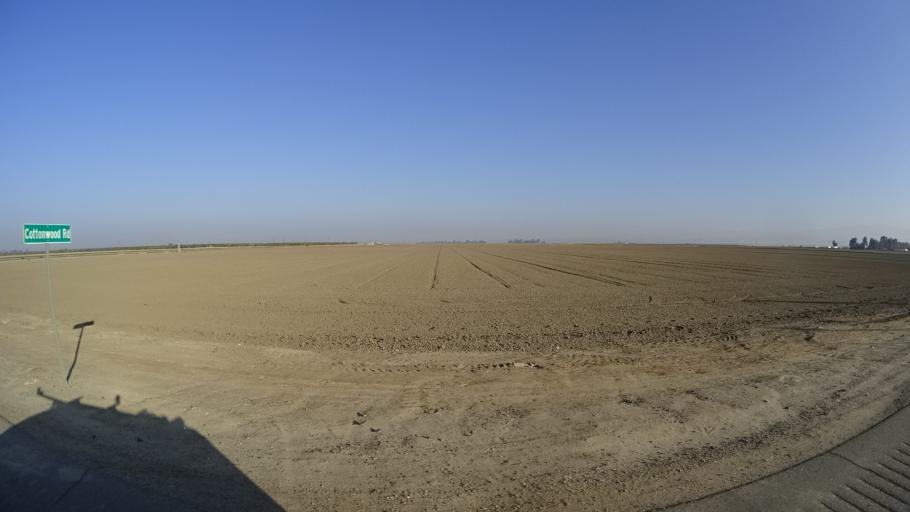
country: US
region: California
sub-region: Kern County
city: Greenfield
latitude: 35.2669
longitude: -118.9835
